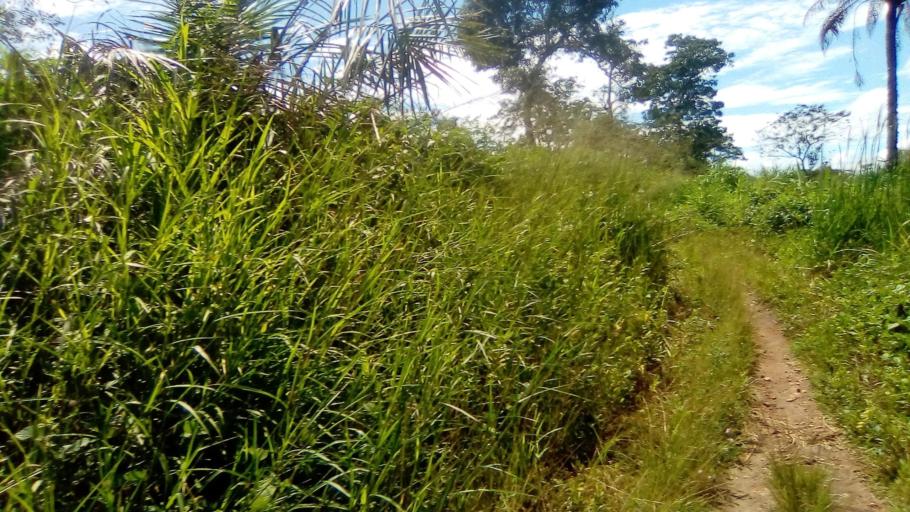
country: SL
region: Eastern Province
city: Simbakoro
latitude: 8.6325
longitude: -11.0016
